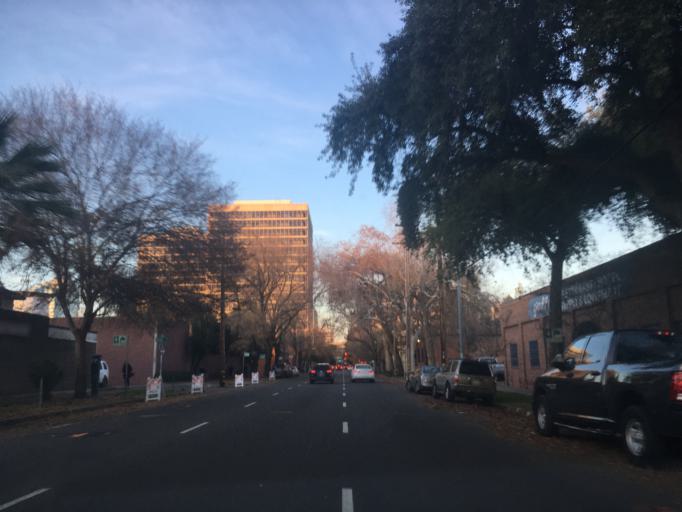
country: US
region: California
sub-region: Sacramento County
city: Sacramento
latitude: 38.5713
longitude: -121.5003
